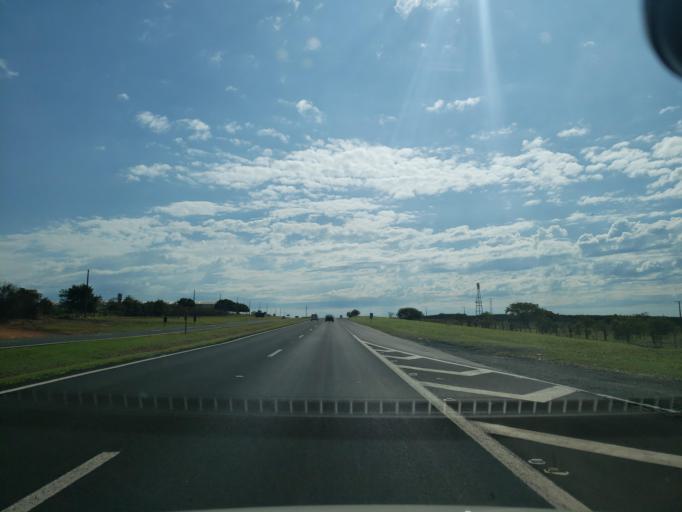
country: BR
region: Sao Paulo
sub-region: Pirajui
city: Pirajui
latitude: -22.0067
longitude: -49.4246
